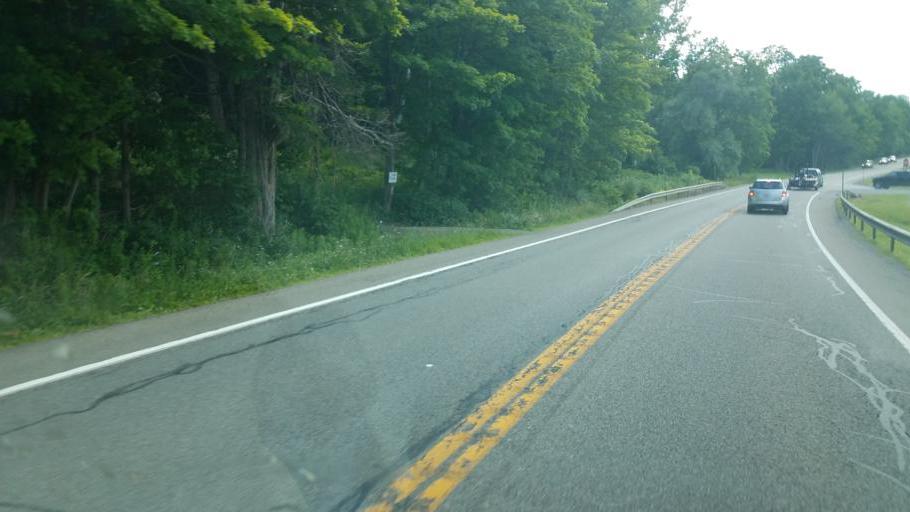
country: US
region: New York
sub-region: Steuben County
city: Bath
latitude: 42.4017
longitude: -77.2139
